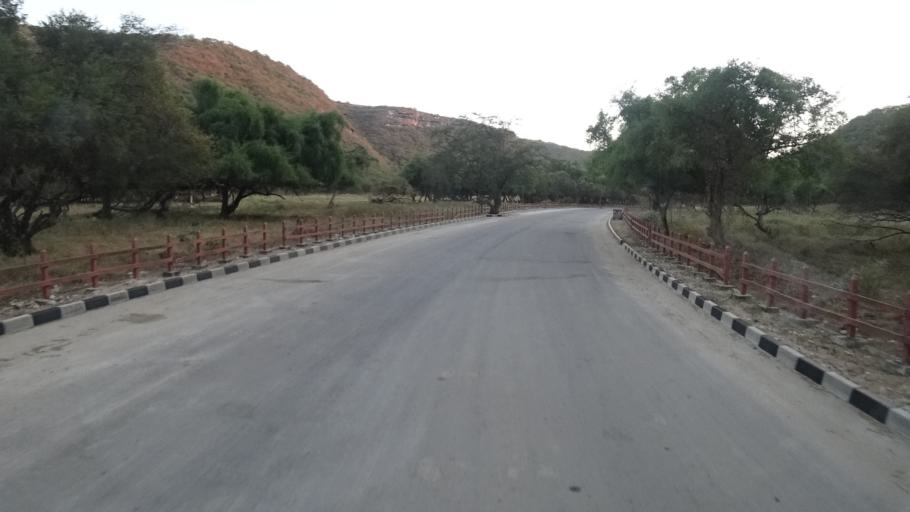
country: OM
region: Zufar
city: Salalah
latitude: 17.1004
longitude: 54.4509
